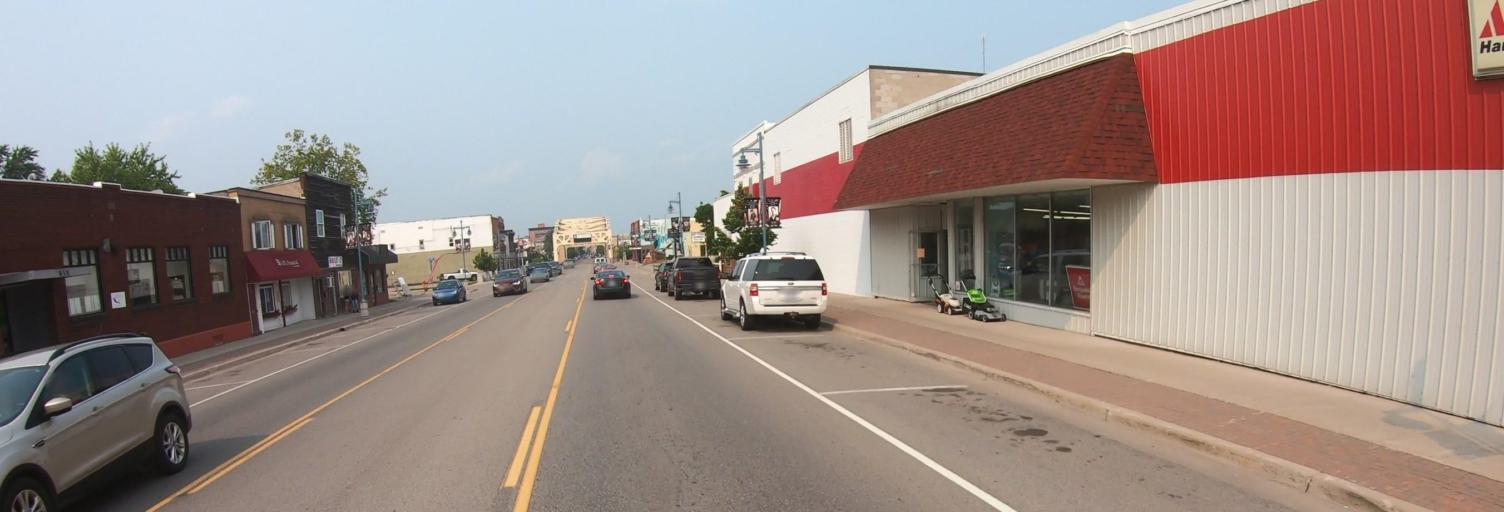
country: US
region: Michigan
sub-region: Chippewa County
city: Sault Ste. Marie
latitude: 46.4933
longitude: -84.3510
